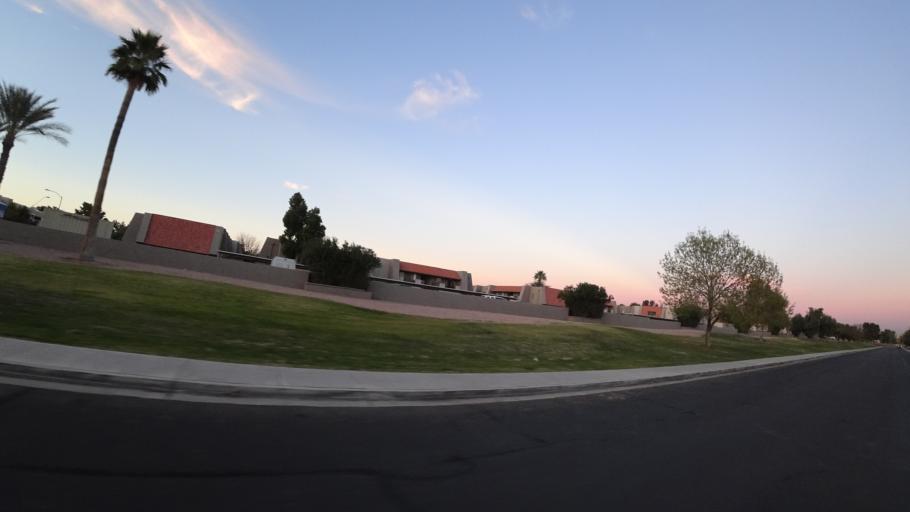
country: US
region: Arizona
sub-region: Maricopa County
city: Scottsdale
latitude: 33.4840
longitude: -111.9171
